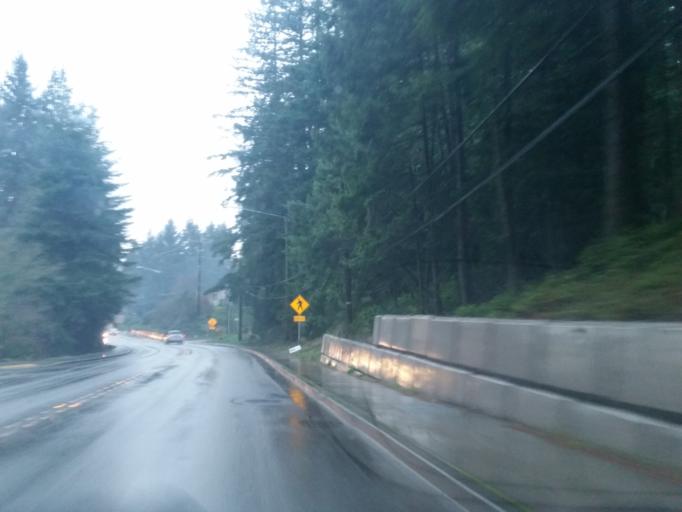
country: US
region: Washington
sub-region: Snohomish County
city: Meadowdale
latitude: 47.8419
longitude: -122.3231
